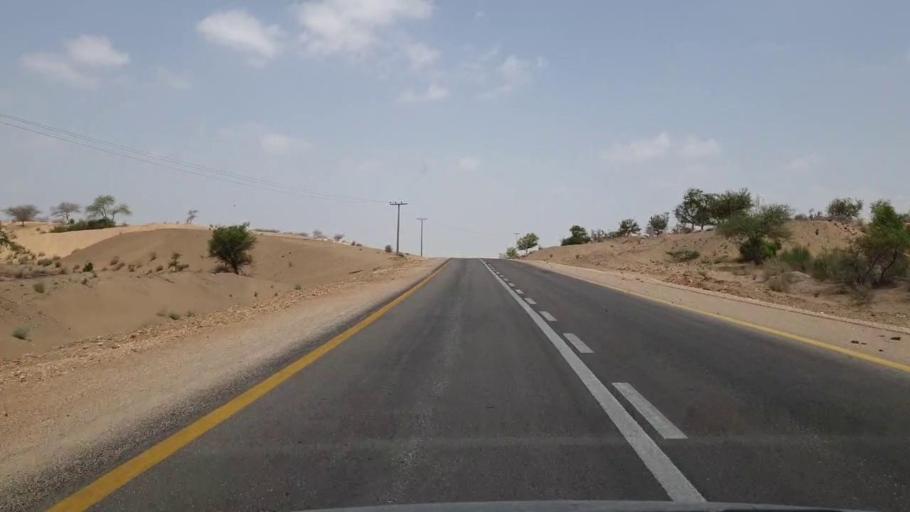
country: PK
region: Sindh
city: Mithi
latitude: 24.7999
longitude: 69.7382
